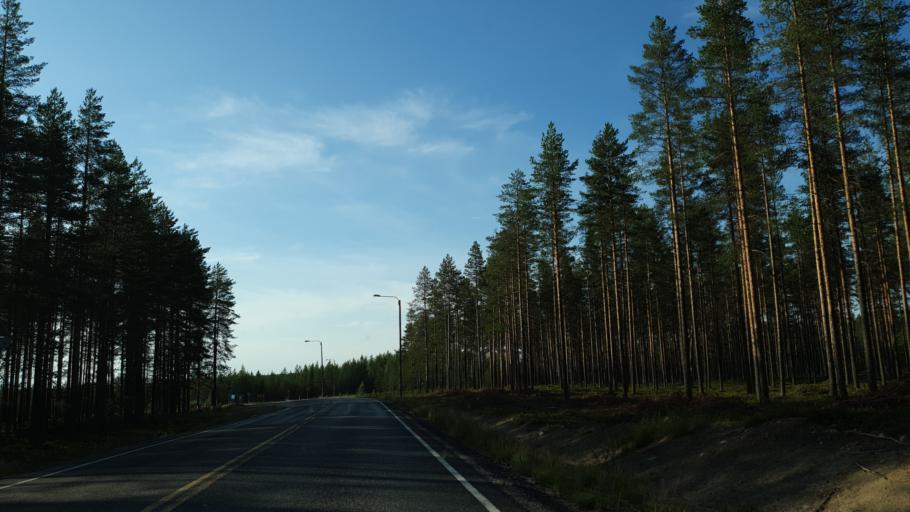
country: FI
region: Kainuu
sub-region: Kehys-Kainuu
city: Kuhmo
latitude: 64.0980
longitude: 29.4754
